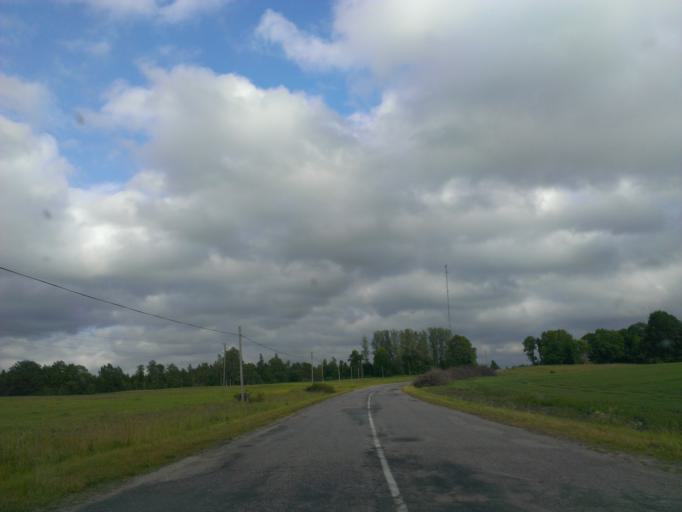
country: LV
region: Aizpute
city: Aizpute
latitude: 56.7223
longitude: 21.7539
